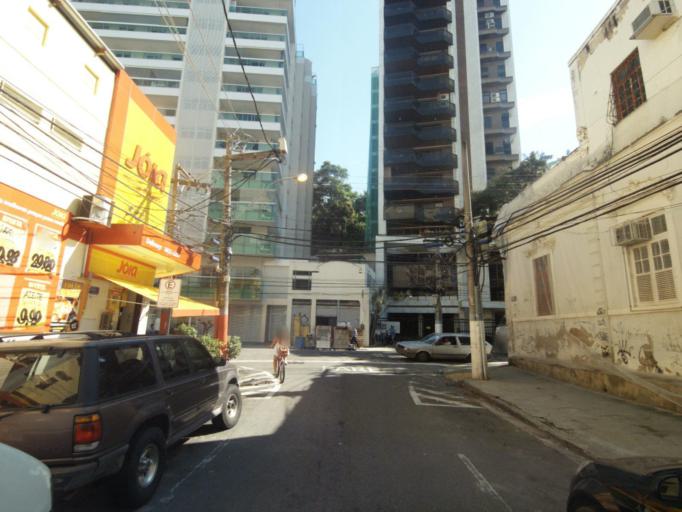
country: BR
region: Rio de Janeiro
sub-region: Niteroi
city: Niteroi
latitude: -22.9016
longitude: -43.1239
